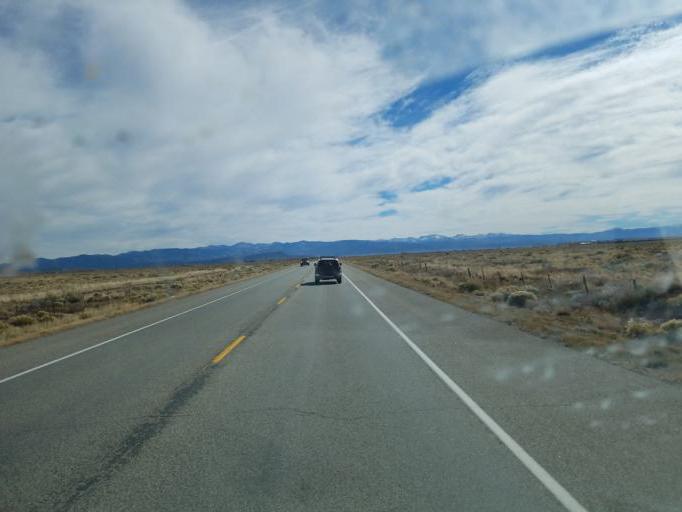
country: US
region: Colorado
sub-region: Costilla County
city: San Luis
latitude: 37.4523
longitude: -105.5463
